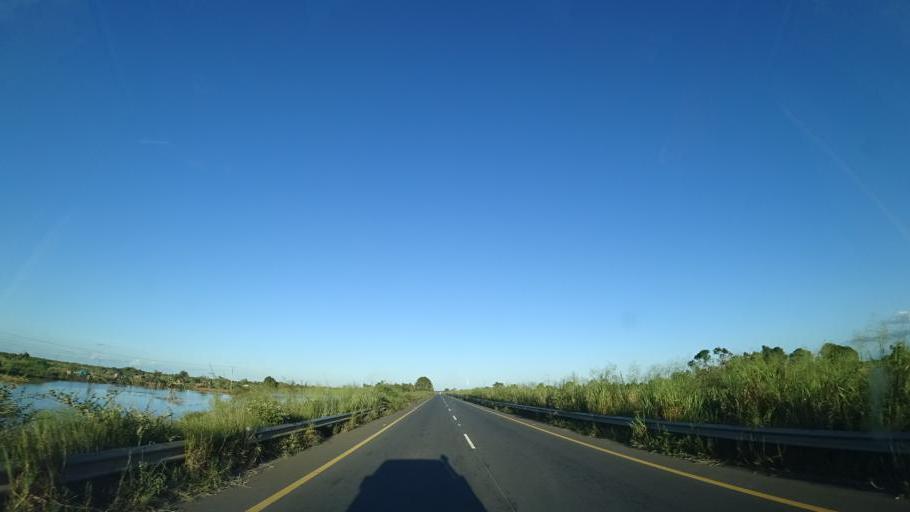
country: MZ
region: Sofala
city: Dondo
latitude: -19.3375
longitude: 34.3321
